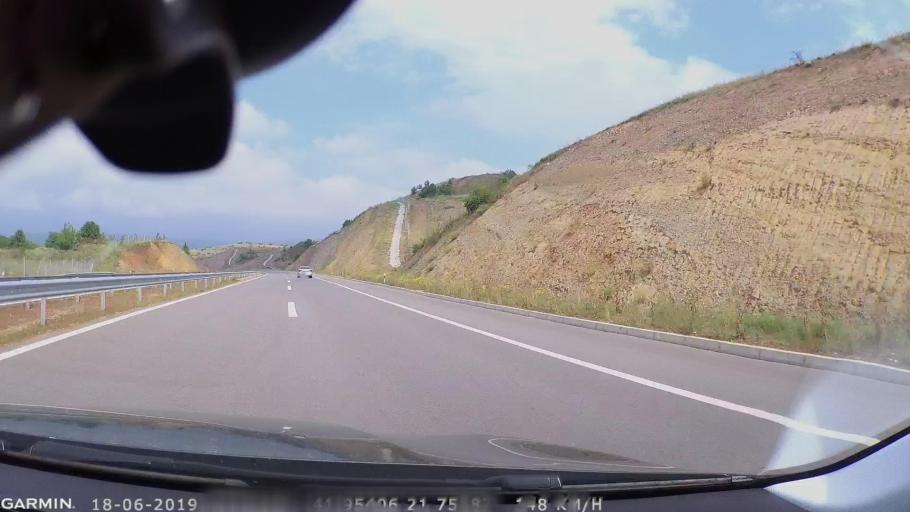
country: MK
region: Sveti Nikole
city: Gorobinci
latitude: 41.9256
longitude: 21.8368
